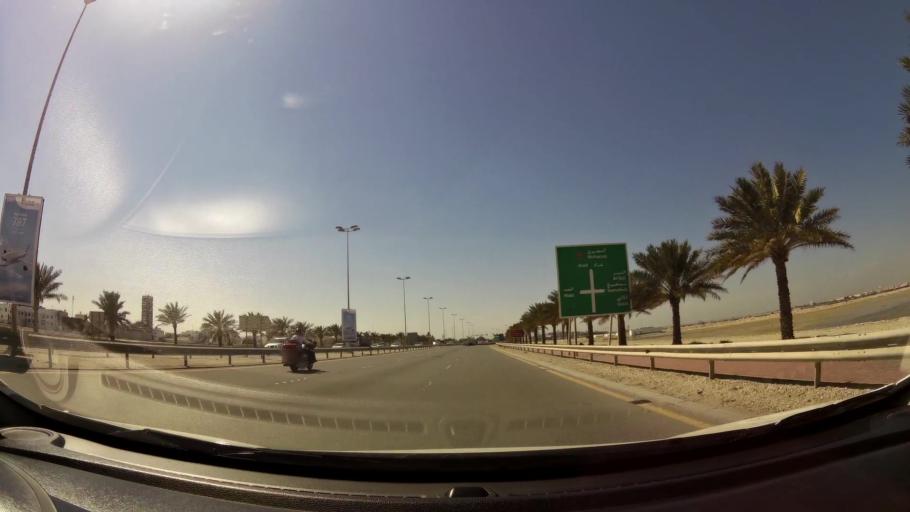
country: BH
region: Muharraq
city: Al Hadd
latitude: 26.2546
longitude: 50.6583
